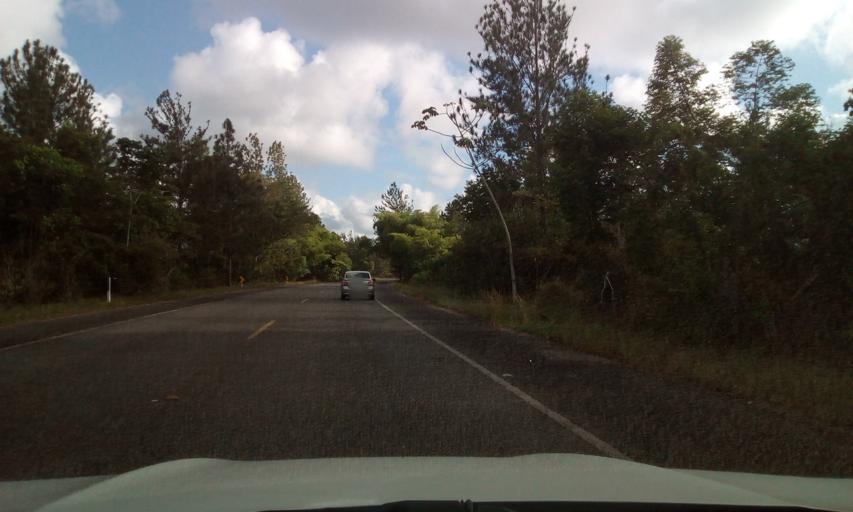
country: BR
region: Bahia
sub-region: Entre Rios
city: Entre Rios
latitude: -12.1539
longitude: -37.8022
